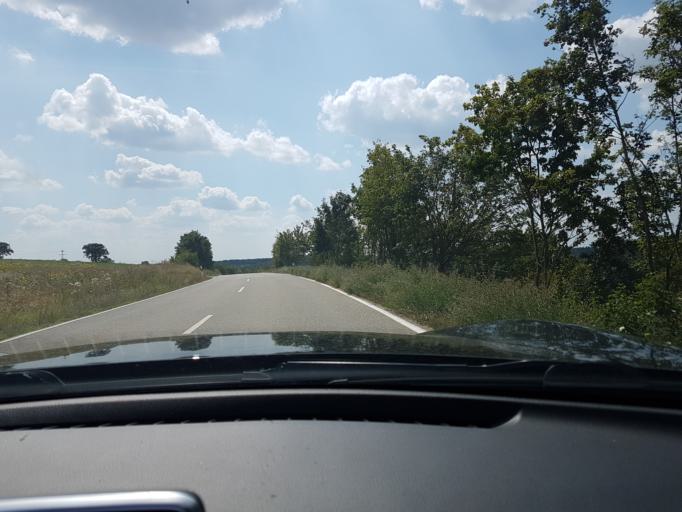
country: DE
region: Baden-Wuerttemberg
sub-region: Karlsruhe Region
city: Limbach
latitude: 49.4259
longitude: 9.2461
